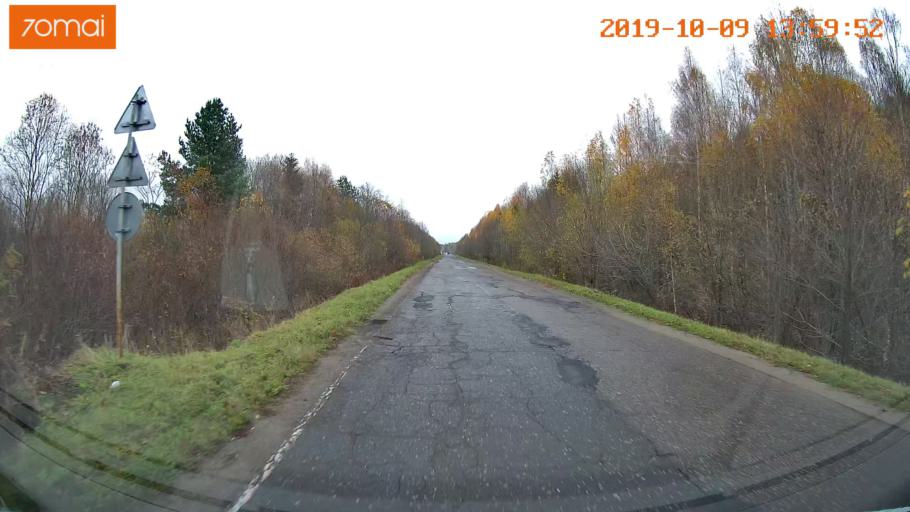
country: RU
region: Kostroma
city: Buy
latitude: 58.4370
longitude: 41.3283
